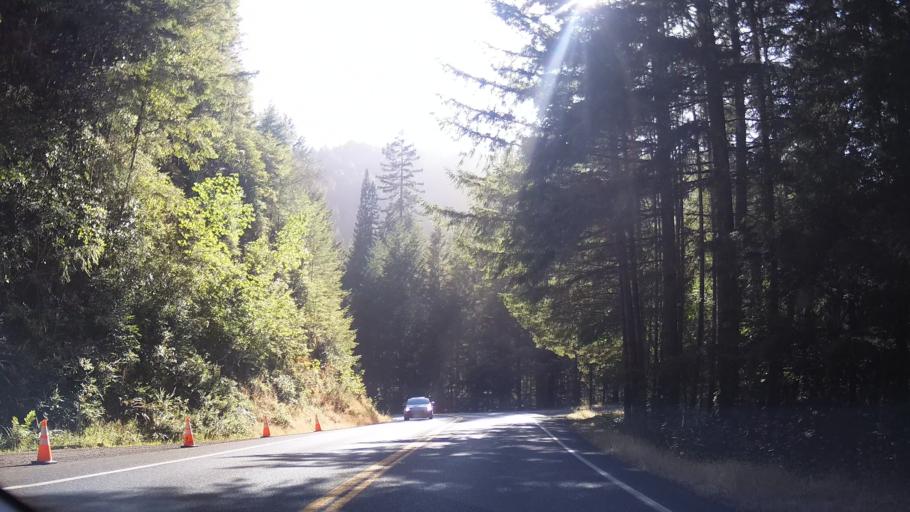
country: US
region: California
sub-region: Mendocino County
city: Brooktrails
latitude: 39.3597
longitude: -123.5071
